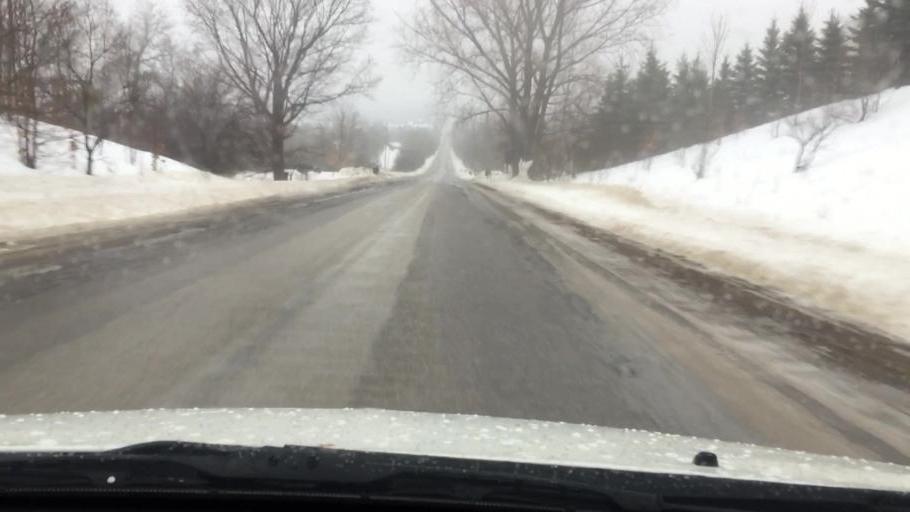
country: US
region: Michigan
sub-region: Charlevoix County
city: East Jordan
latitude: 45.1325
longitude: -85.1571
